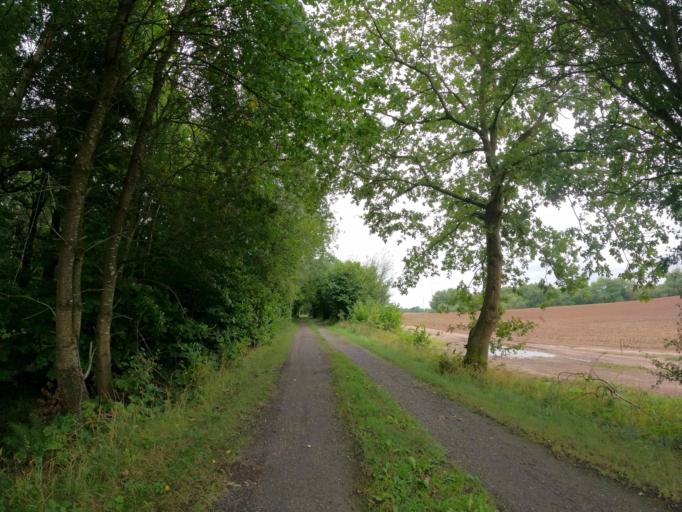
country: DE
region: Mecklenburg-Vorpommern
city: Garz
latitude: 54.3350
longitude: 13.3676
